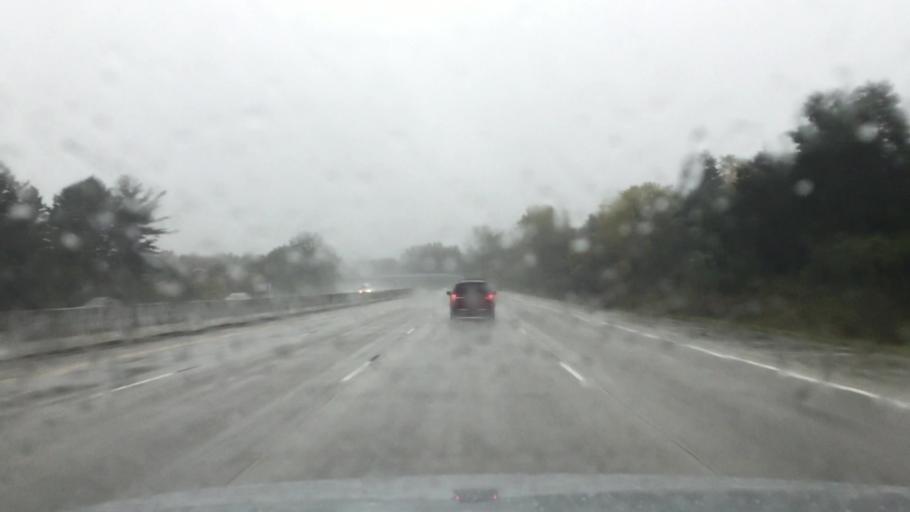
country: US
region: Michigan
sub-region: Saginaw County
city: Bridgeport
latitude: 43.3611
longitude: -83.8672
